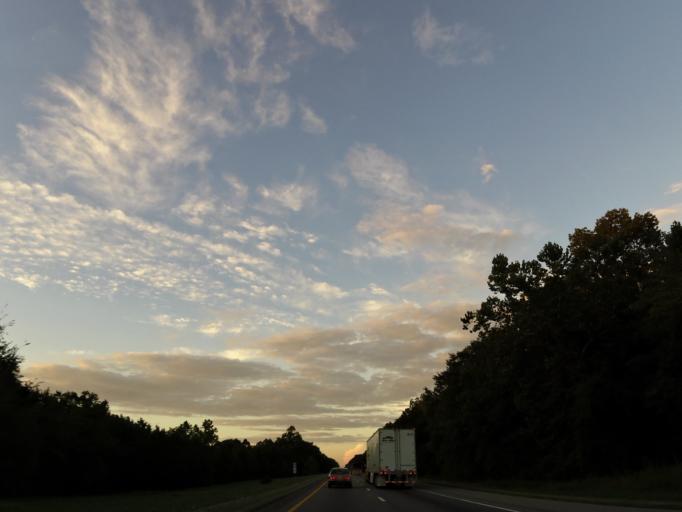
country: US
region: Tennessee
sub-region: Monroe County
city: Sweetwater
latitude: 35.5655
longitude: -84.5477
